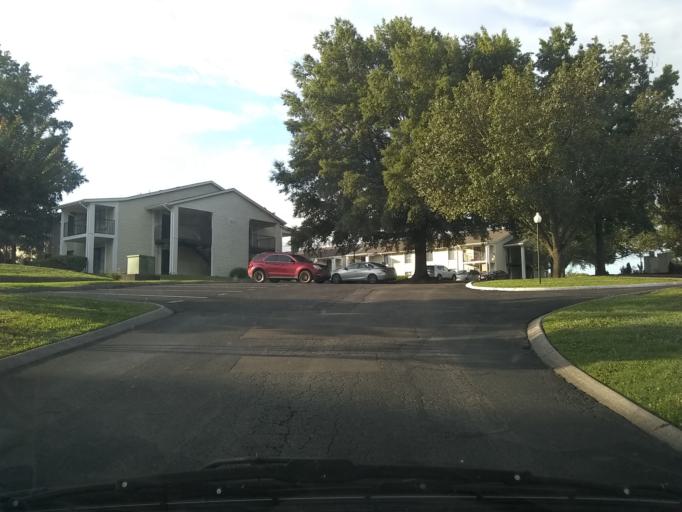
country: US
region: Tennessee
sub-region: Davidson County
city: Nashville
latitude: 36.1328
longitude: -86.7033
